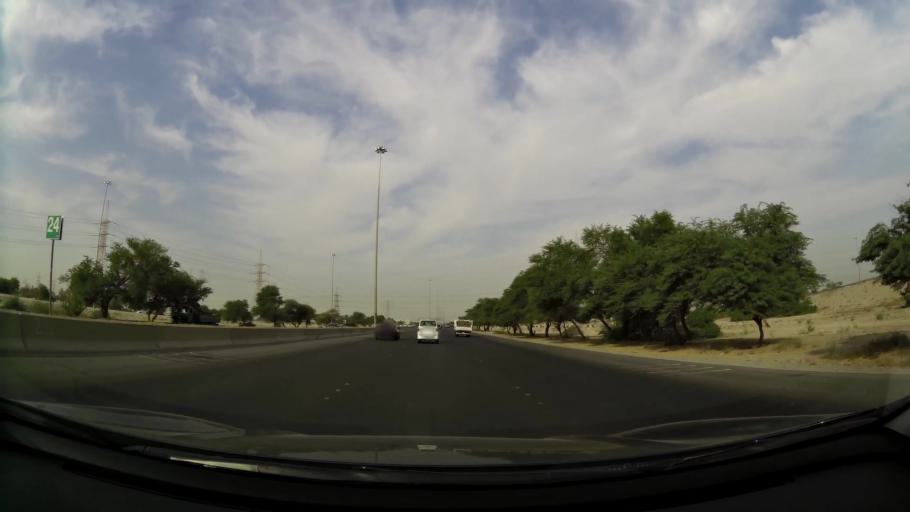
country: KW
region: Al Asimah
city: Ar Rabiyah
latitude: 29.2656
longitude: 47.8382
